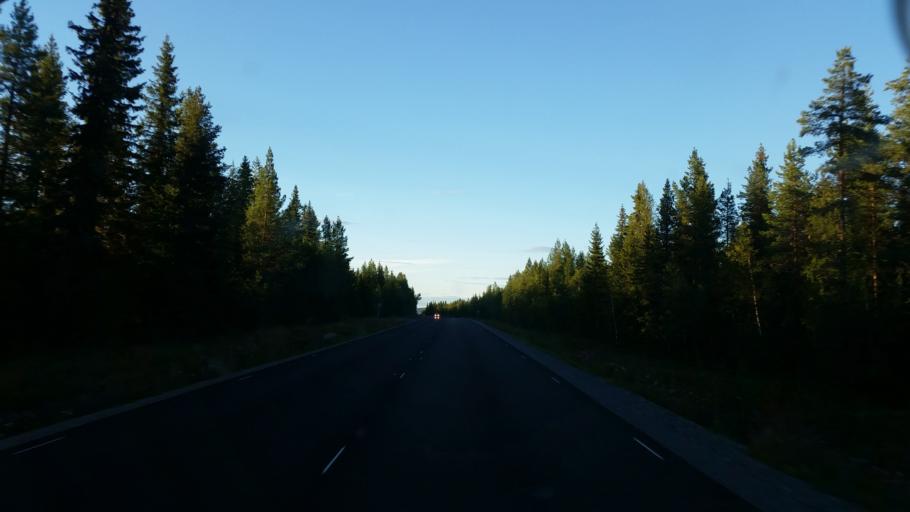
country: SE
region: Vaesterbotten
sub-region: Vilhelmina Kommun
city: Vilhelmina
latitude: 64.7687
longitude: 16.7496
